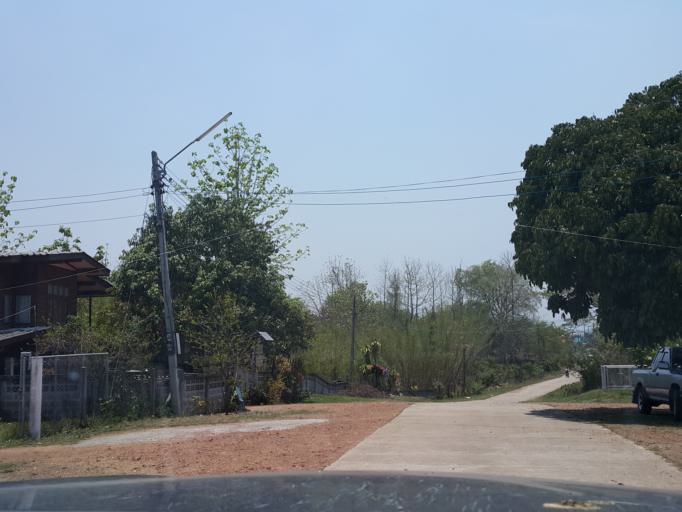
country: TH
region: Lampang
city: Thoen
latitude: 17.6363
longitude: 99.2699
